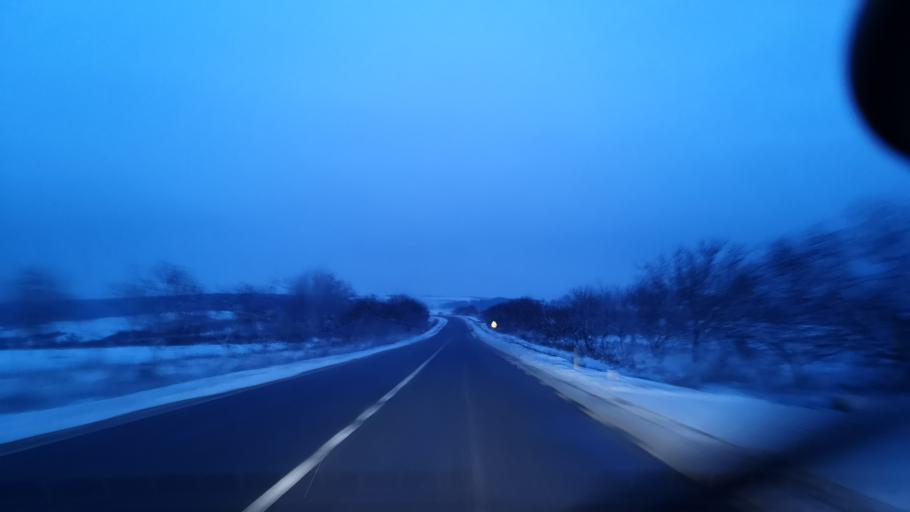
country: MD
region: Rezina
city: Saharna
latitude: 47.6129
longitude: 28.8312
